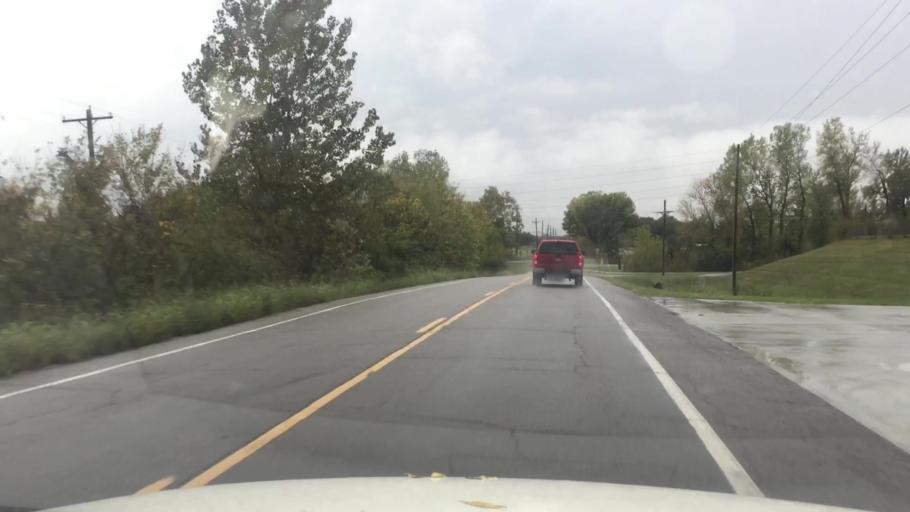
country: US
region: Missouri
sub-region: Boone County
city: Columbia
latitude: 38.8860
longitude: -92.4425
